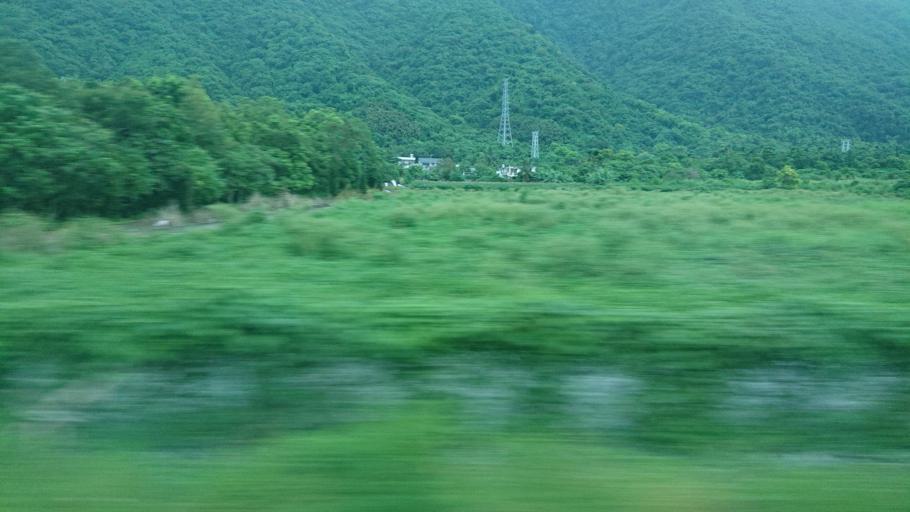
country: TW
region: Taiwan
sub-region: Hualien
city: Hualian
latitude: 24.1125
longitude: 121.6235
